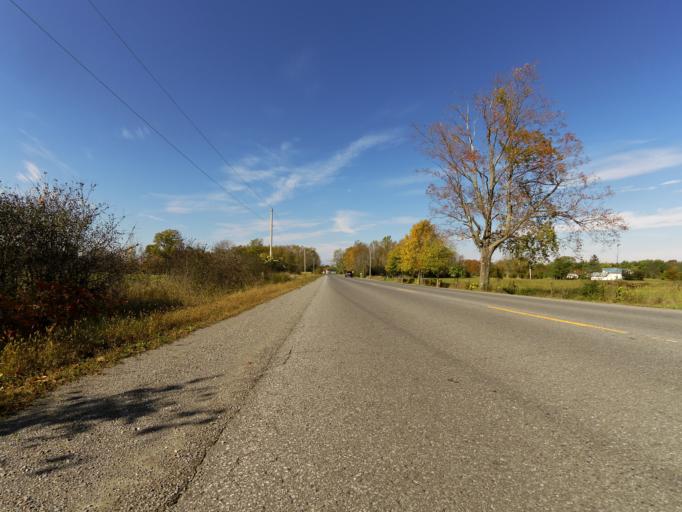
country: CA
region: Ontario
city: Prince Edward
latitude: 44.0154
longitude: -77.3160
